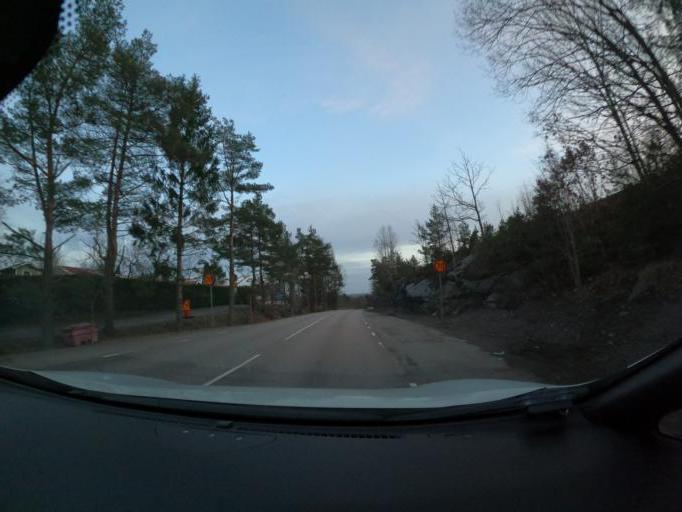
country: SE
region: Vaestra Goetaland
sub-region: Harryda Kommun
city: Molnlycke
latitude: 57.6484
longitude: 12.1584
